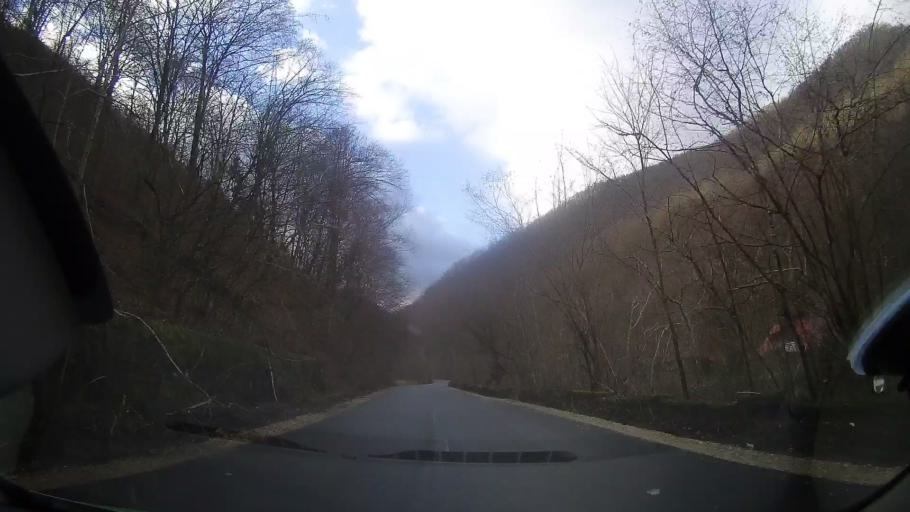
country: RO
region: Cluj
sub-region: Comuna Valea Ierii
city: Valea Ierii
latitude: 46.6909
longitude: 23.2986
